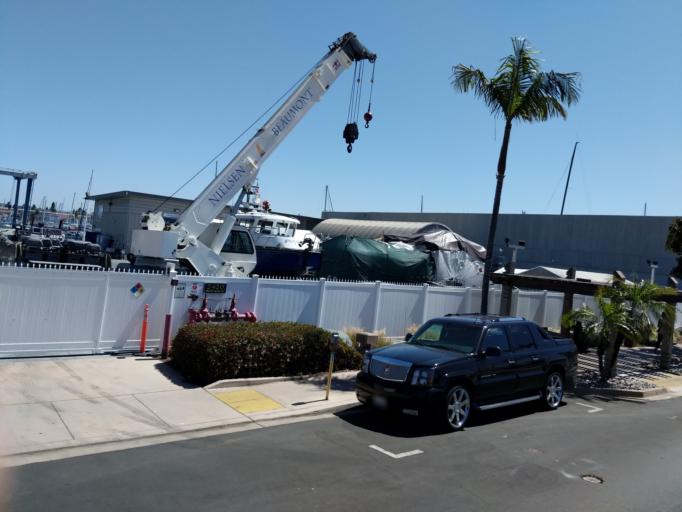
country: US
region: California
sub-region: San Diego County
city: Coronado
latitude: 32.7195
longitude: -117.2258
